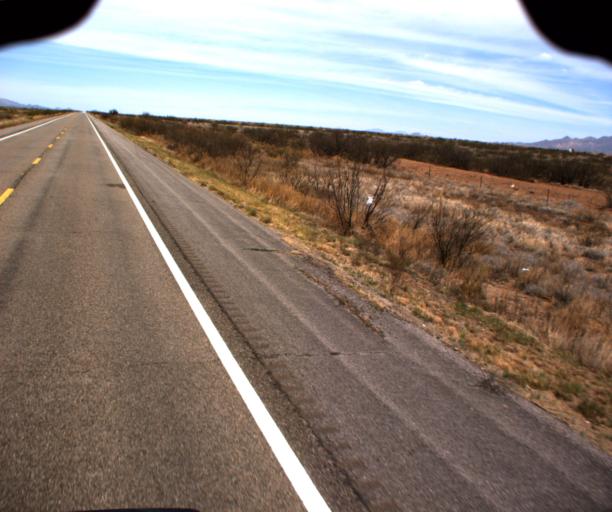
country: US
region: Arizona
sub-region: Cochise County
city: Pirtleville
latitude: 31.5049
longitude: -109.6375
